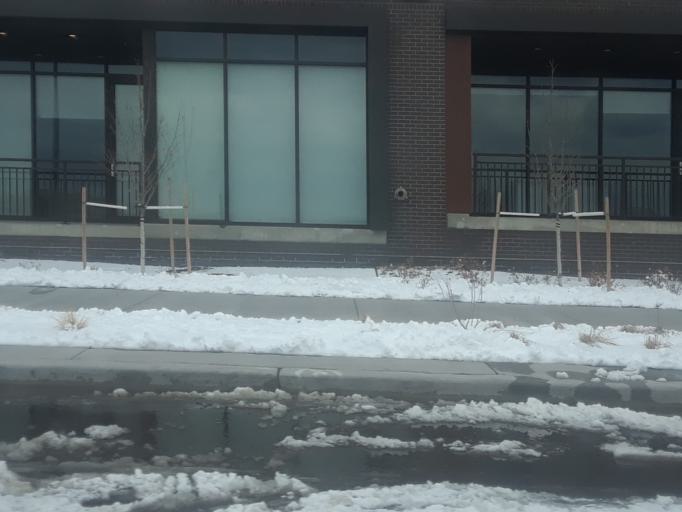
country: US
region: Colorado
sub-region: Arapahoe County
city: Centennial
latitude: 39.5748
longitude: -104.8791
